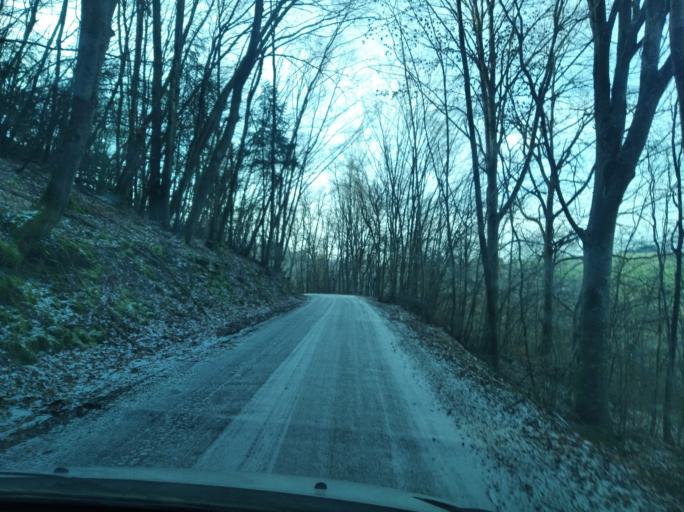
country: FR
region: Auvergne
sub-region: Departement de l'Allier
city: Le Mayet-de-Montagne
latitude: 46.1732
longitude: 3.7404
